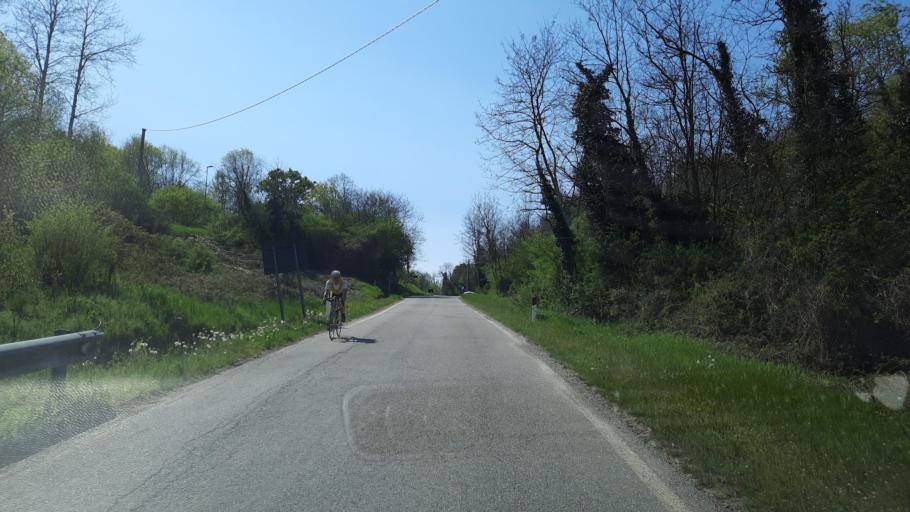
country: IT
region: Piedmont
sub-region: Provincia di Torino
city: Valentino
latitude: 45.1535
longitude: 8.1276
